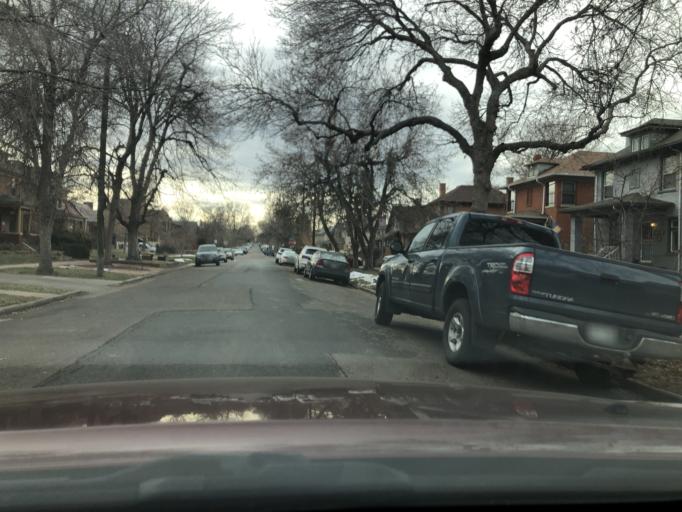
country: US
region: Colorado
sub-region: Denver County
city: Denver
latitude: 39.7579
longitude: -104.9622
